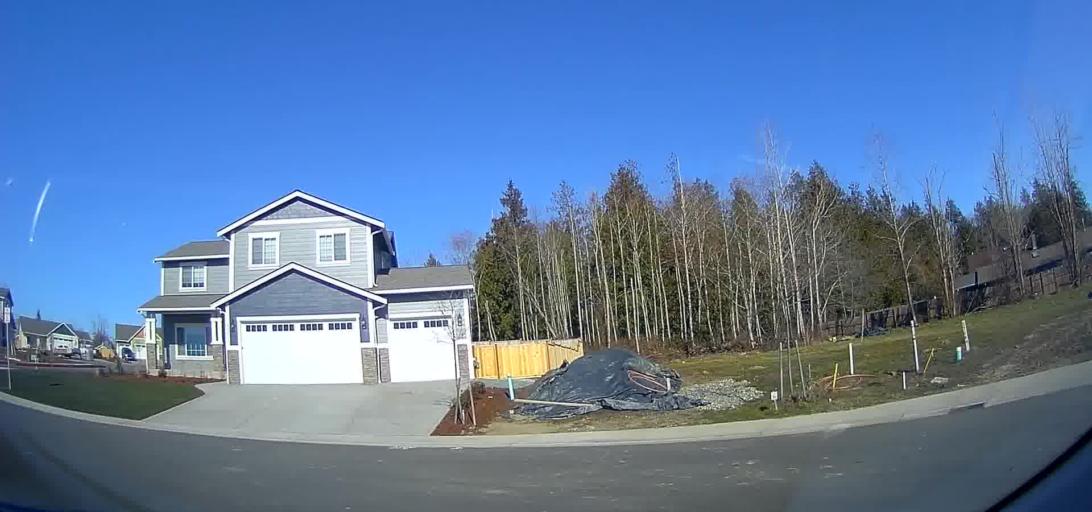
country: US
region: Washington
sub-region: Skagit County
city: Mount Vernon
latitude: 48.4412
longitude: -122.2980
